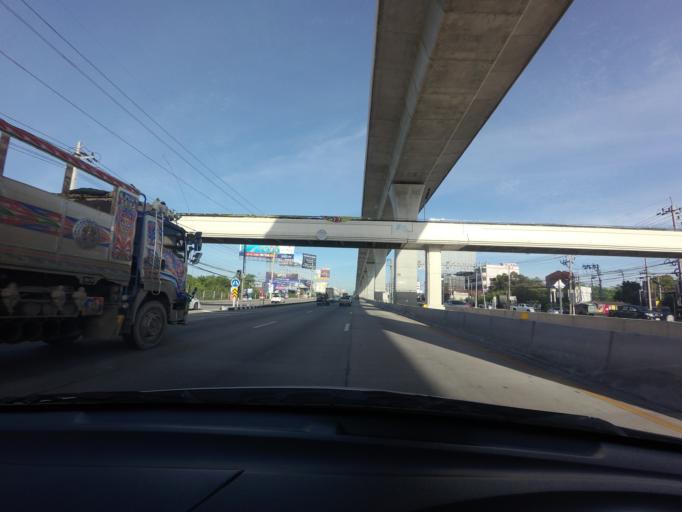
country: TH
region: Nonthaburi
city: Bang Bua Thong
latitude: 13.8752
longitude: 100.4273
